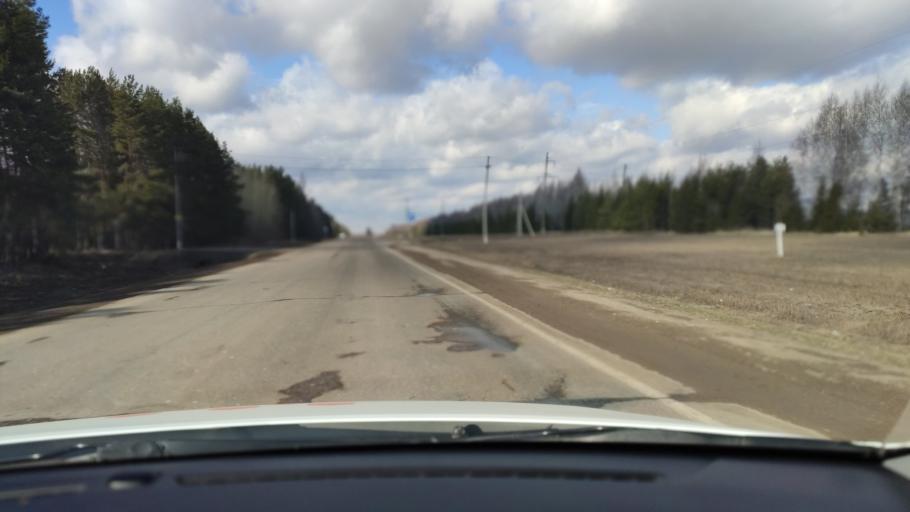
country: RU
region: Tatarstan
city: Vysokaya Gora
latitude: 56.0605
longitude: 49.2054
